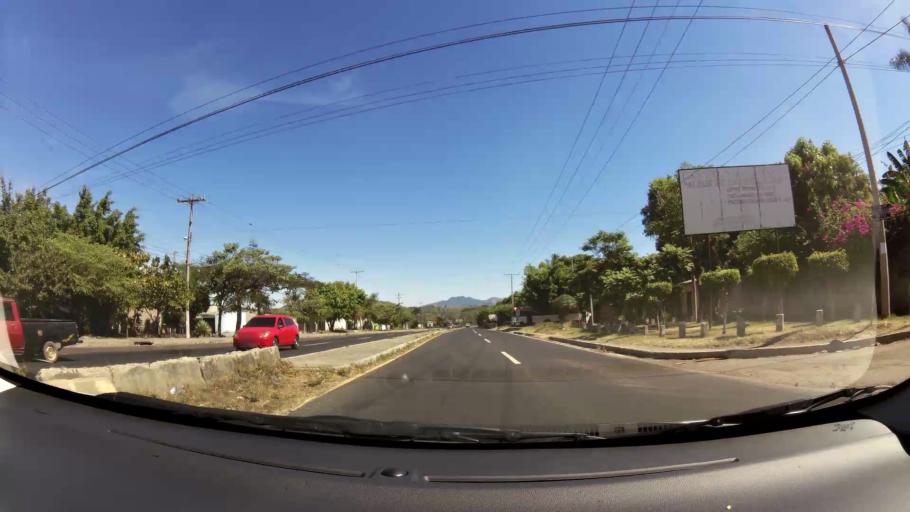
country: SV
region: La Libertad
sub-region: Distrito de Quezaltepeque
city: Quezaltepeque
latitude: 13.8258
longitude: -89.2687
